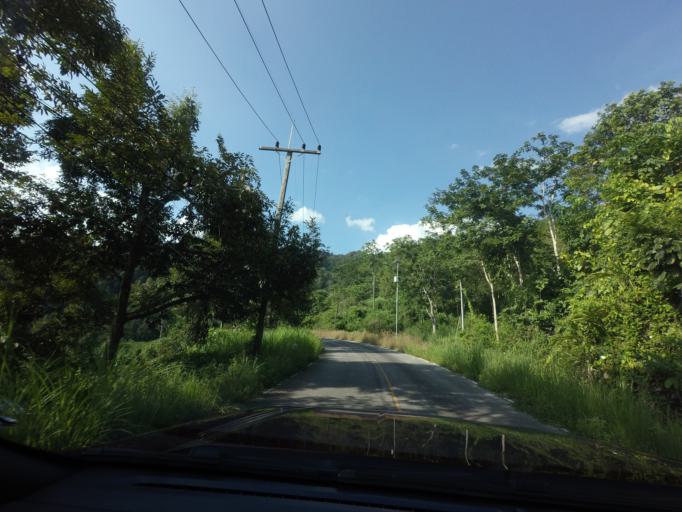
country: TH
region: Yala
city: Than To
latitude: 6.1234
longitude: 101.3015
